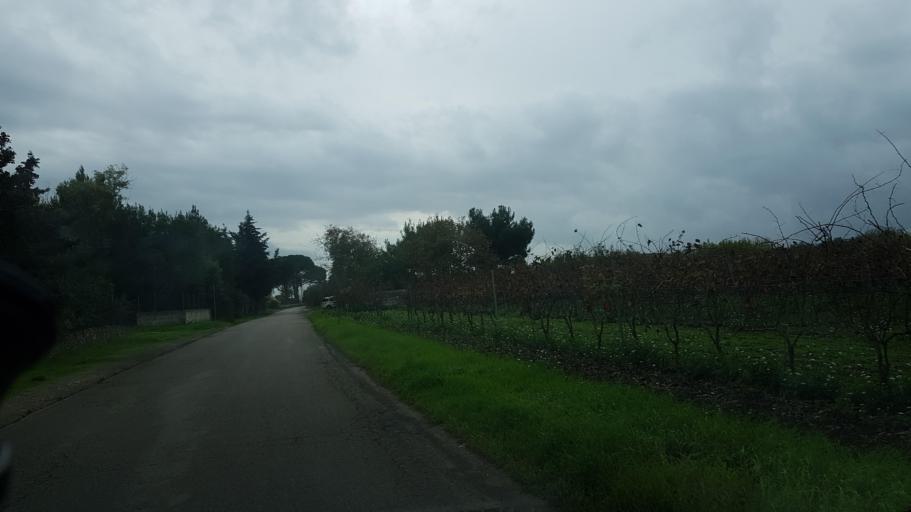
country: IT
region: Apulia
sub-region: Provincia di Lecce
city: Campi Salentina
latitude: 40.3877
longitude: 18.0211
